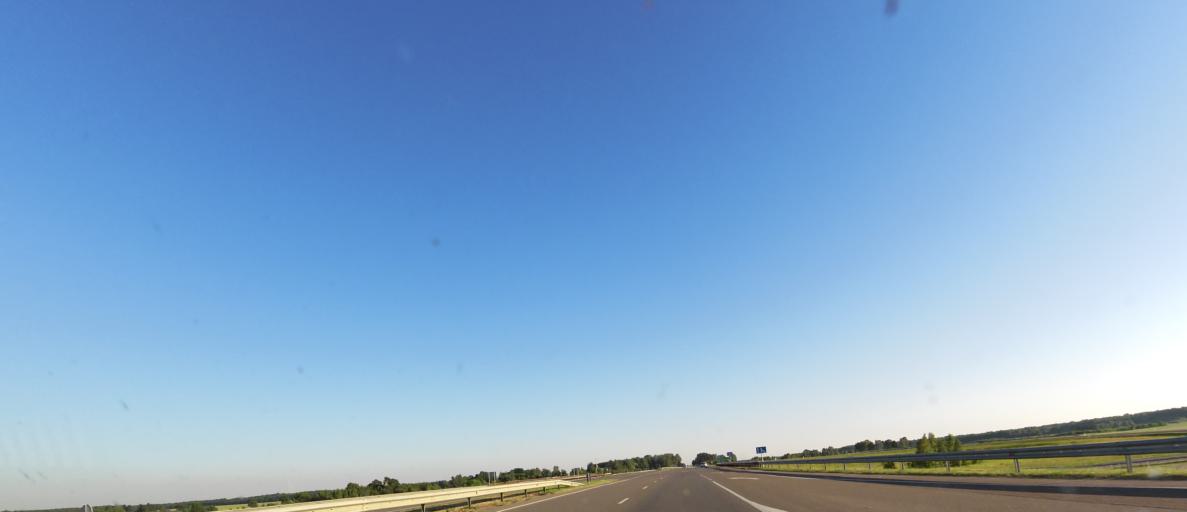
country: LT
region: Panevezys
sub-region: Panevezys City
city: Panevezys
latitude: 55.6657
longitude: 24.3632
